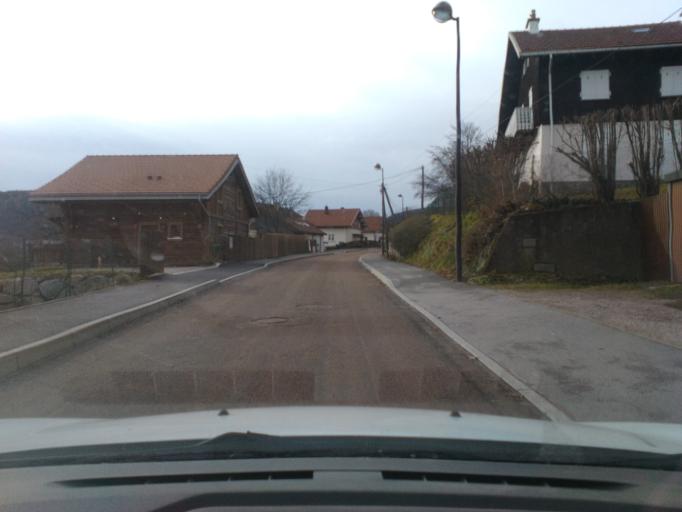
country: FR
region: Lorraine
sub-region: Departement des Vosges
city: Gerardmer
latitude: 48.0752
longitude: 6.8723
